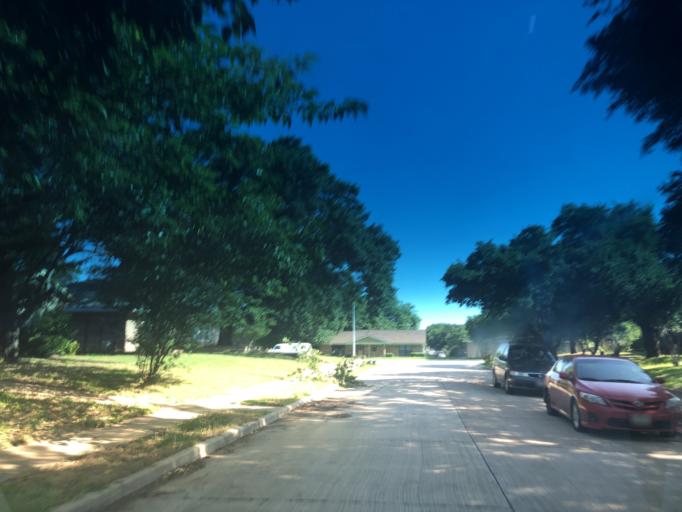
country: US
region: Texas
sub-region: Dallas County
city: Grand Prairie
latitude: 32.7172
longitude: -97.0170
